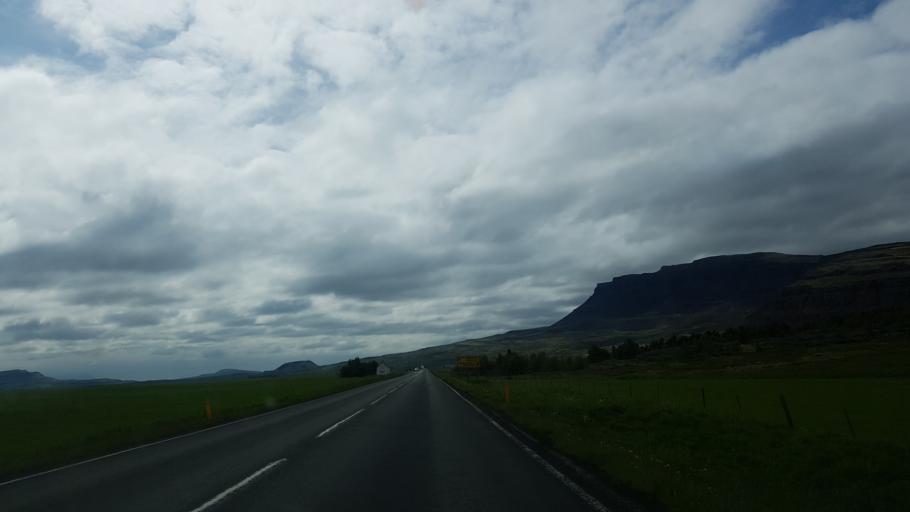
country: IS
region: West
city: Borgarnes
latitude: 64.8029
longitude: -21.4560
